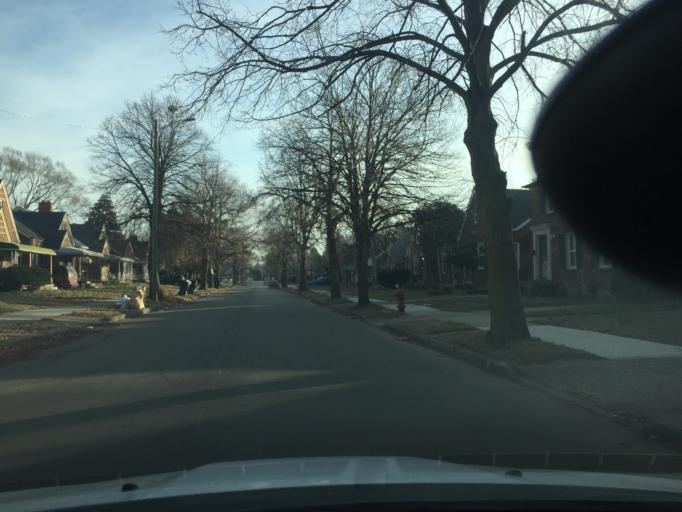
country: US
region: Michigan
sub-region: Macomb County
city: Eastpointe
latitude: 42.4338
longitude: -82.9644
